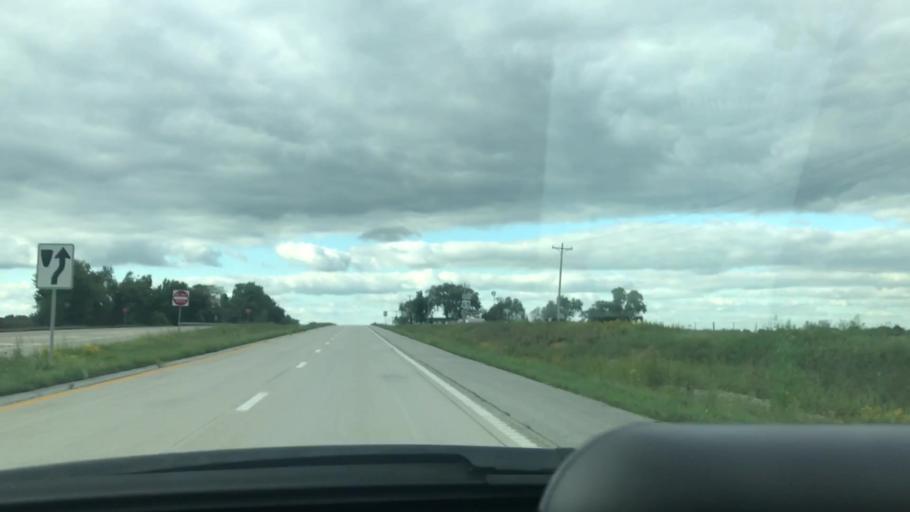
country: US
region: Missouri
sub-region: Benton County
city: Lincoln
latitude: 38.3659
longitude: -93.3389
